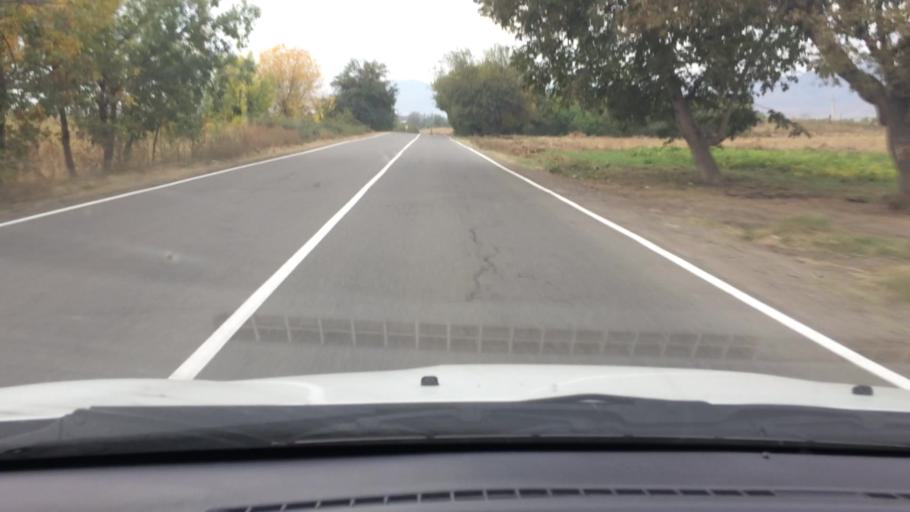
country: GE
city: Naghvarevi
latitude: 41.3190
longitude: 44.7953
